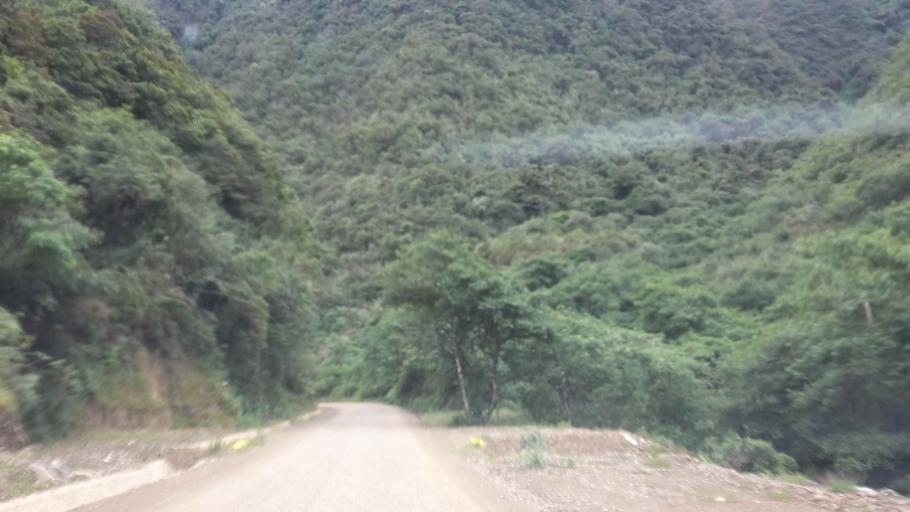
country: BO
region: Cochabamba
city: Totora
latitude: -17.5595
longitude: -65.2701
